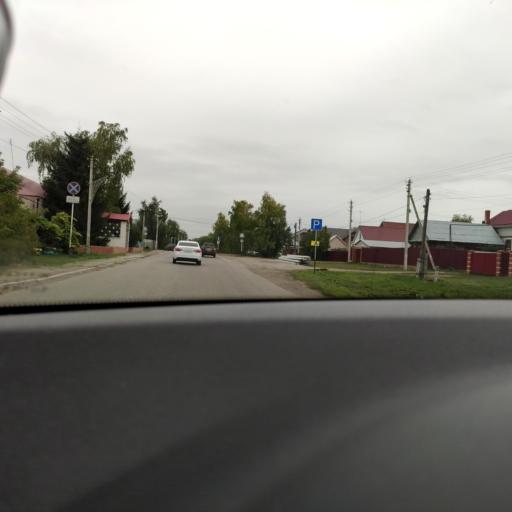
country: RU
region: Samara
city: Krasnyy Yar
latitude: 53.4950
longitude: 50.3860
